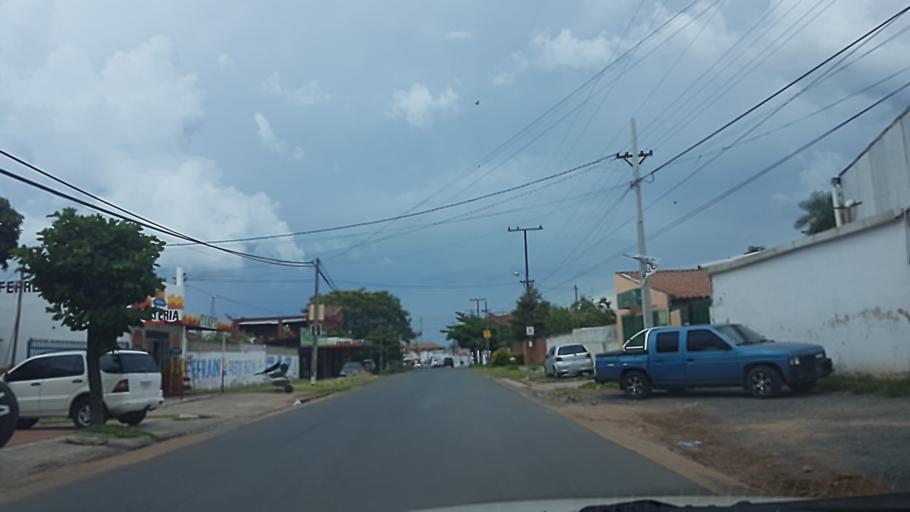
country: PY
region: Central
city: Colonia Mariano Roque Alonso
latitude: -25.2142
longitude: -57.5273
